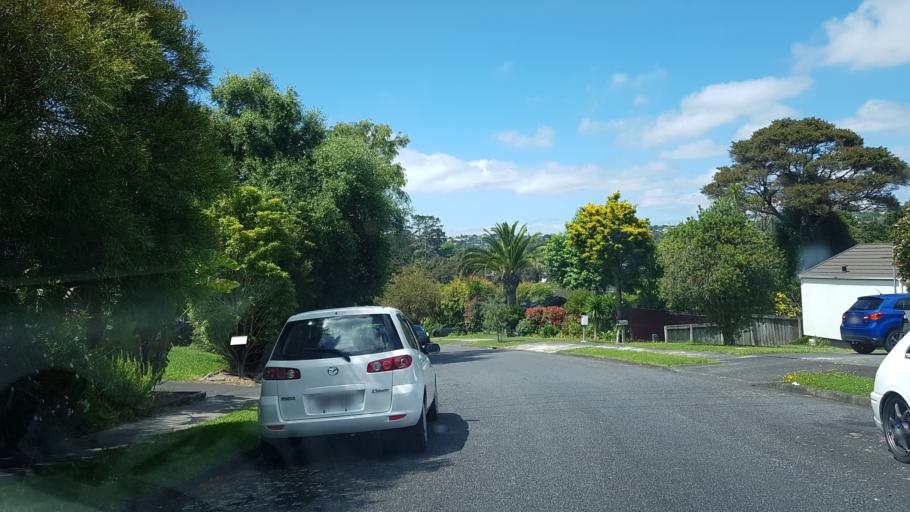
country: NZ
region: Auckland
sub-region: Auckland
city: North Shore
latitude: -36.7929
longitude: 174.7142
